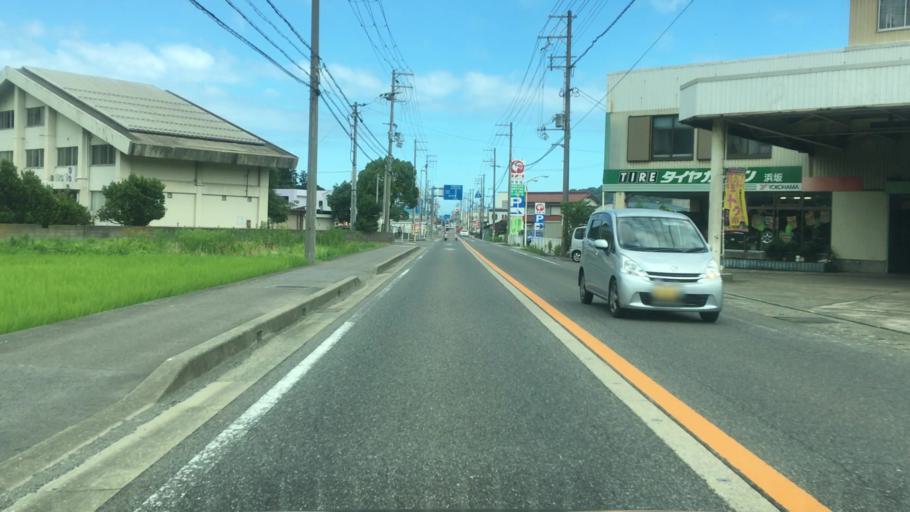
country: JP
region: Tottori
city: Tottori
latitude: 35.6159
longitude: 134.4650
